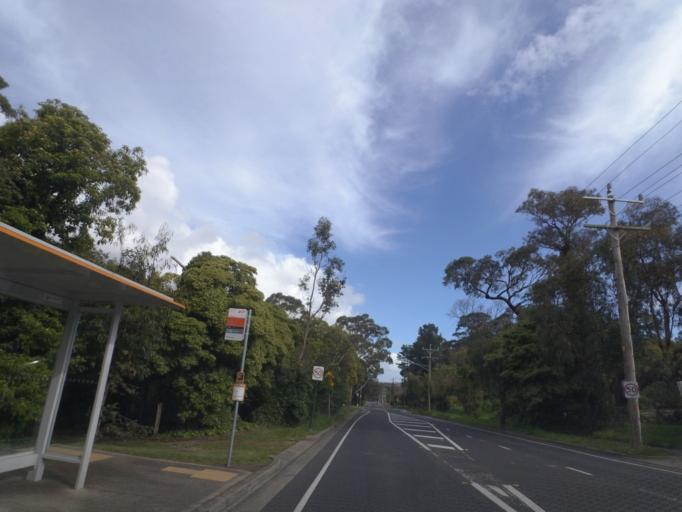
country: AU
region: Victoria
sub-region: Whitehorse
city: Vermont
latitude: -37.8458
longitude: 145.1894
